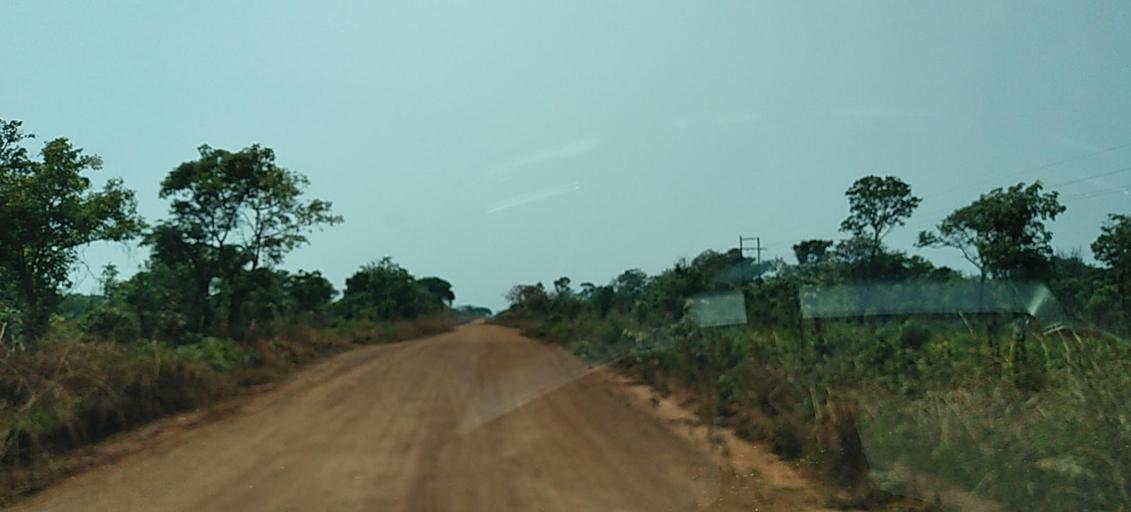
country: ZM
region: North-Western
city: Kansanshi
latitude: -12.0062
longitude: 26.5415
